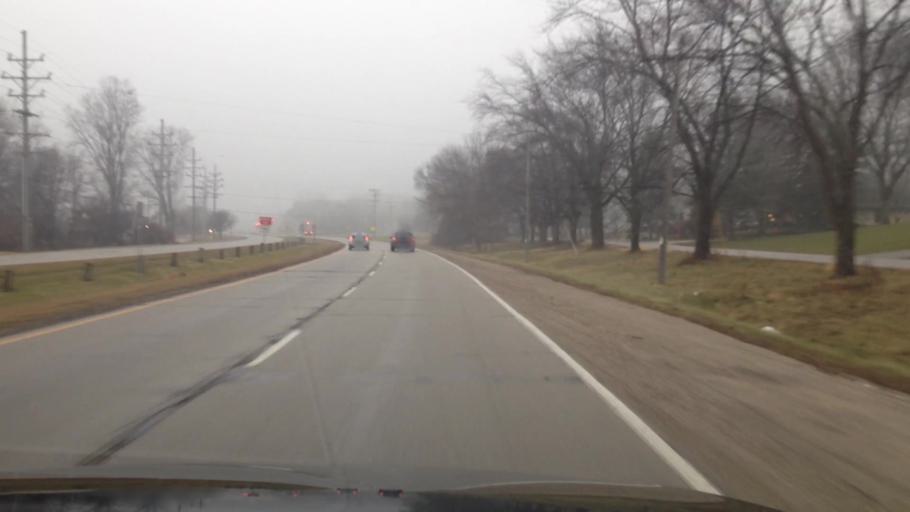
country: US
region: Wisconsin
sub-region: Milwaukee County
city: Hales Corners
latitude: 42.9285
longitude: -88.0535
